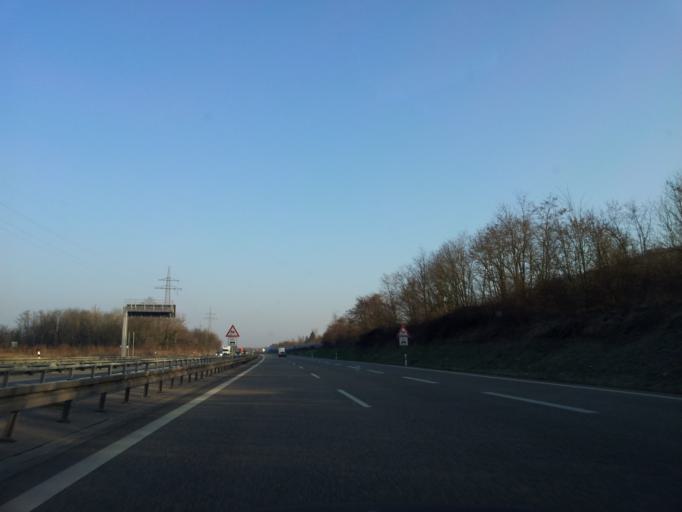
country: FR
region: Alsace
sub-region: Departement du Haut-Rhin
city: Kembs
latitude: 47.6800
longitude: 7.5233
